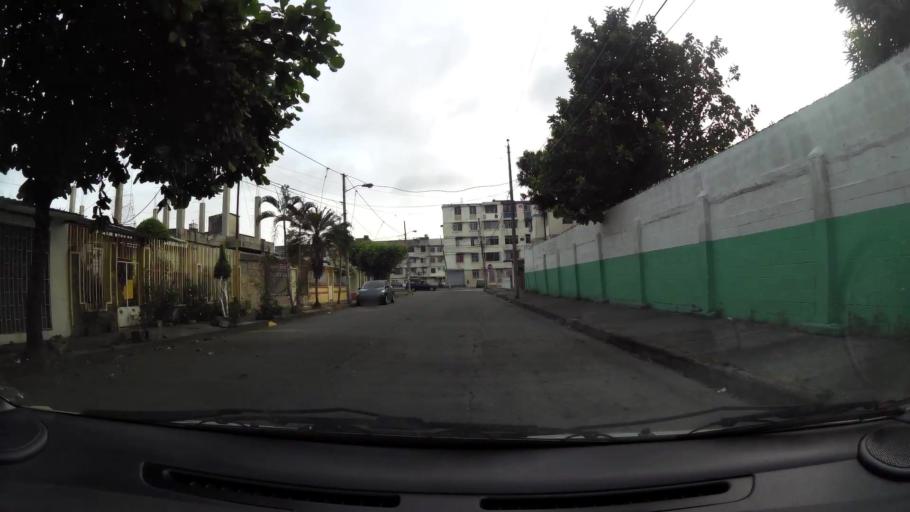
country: EC
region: Guayas
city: Eloy Alfaro
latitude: -2.1723
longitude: -79.8857
